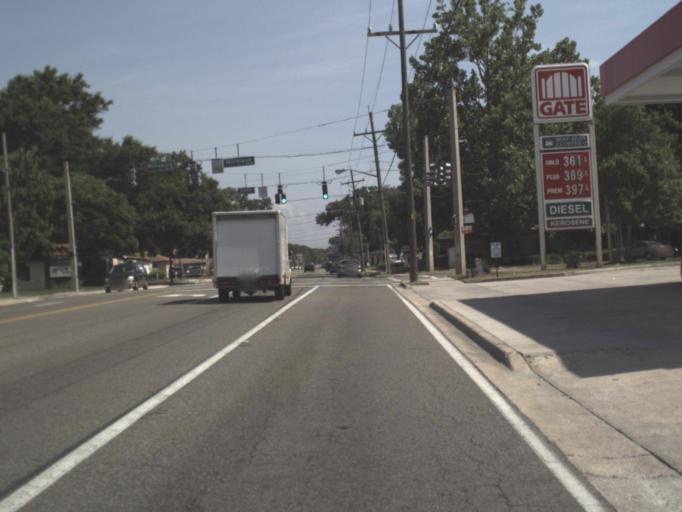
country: US
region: Florida
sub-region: Duval County
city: Jacksonville
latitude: 30.3381
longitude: -81.6025
